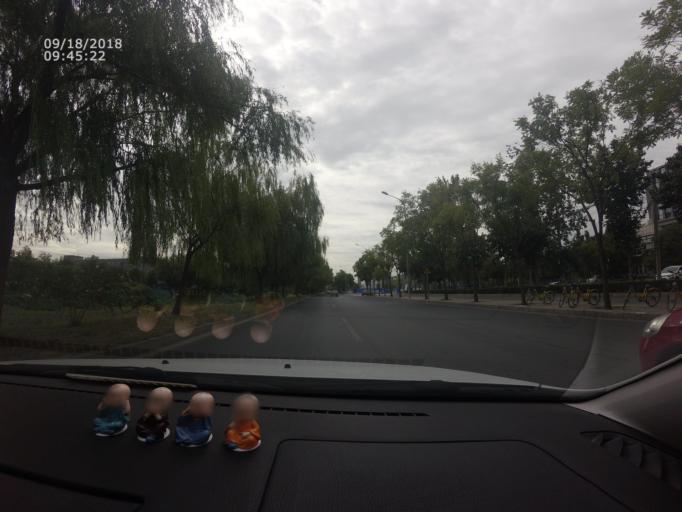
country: CN
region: Beijing
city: Xibeiwang
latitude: 40.0706
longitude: 116.2381
